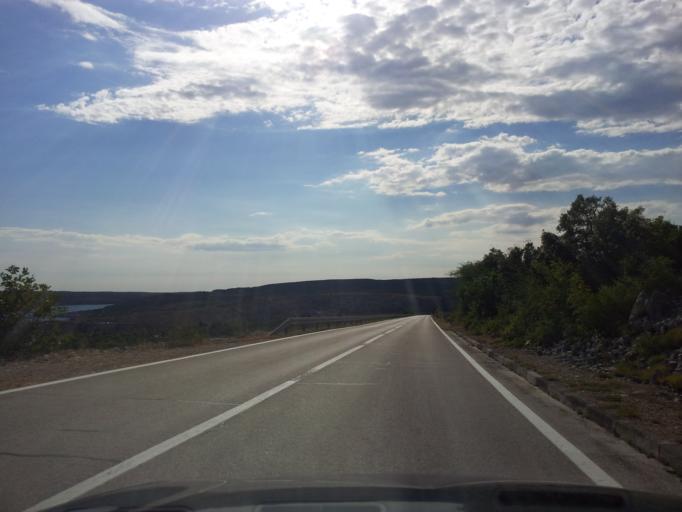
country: HR
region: Zadarska
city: Pridraga
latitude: 44.2281
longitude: 15.5440
